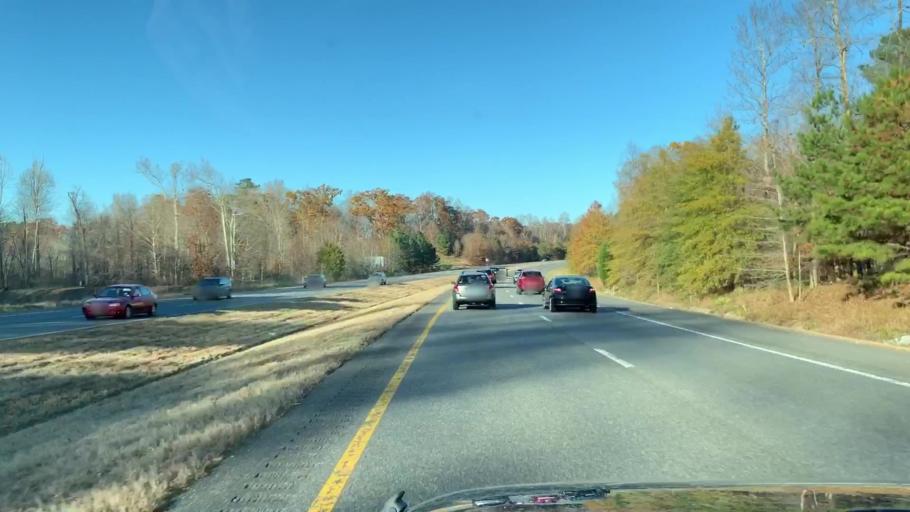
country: US
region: Virginia
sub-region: James City County
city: Williamsburg
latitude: 37.2906
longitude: -76.7524
